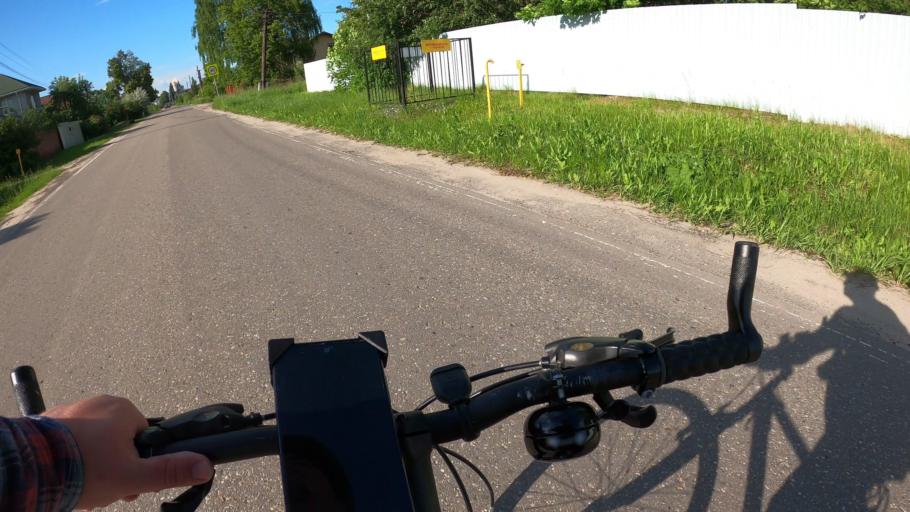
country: RU
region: Moskovskaya
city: Ashitkovo
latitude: 55.4341
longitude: 38.6040
